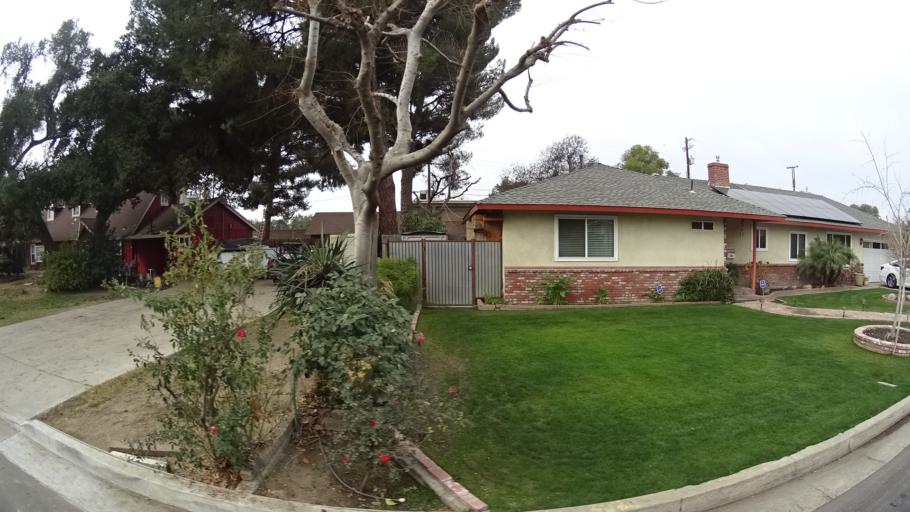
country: US
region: California
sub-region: Kern County
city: Bakersfield
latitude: 35.3571
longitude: -119.0378
